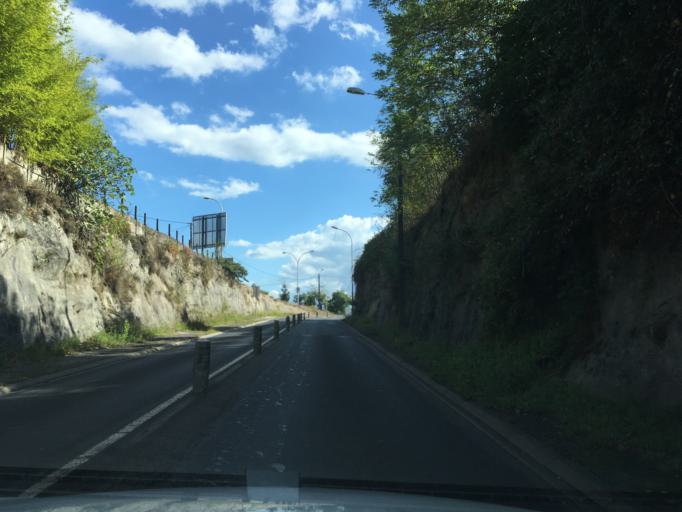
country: FR
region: Limousin
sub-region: Departement de la Correze
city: Brive-la-Gaillarde
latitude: 45.1424
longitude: 1.5491
